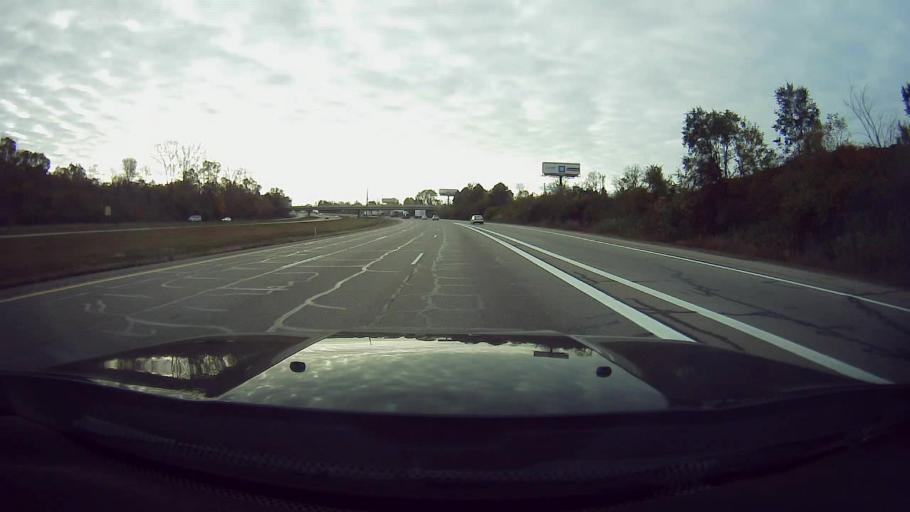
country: US
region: Michigan
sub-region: Wayne County
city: Romulus
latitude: 42.2183
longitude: -83.4118
